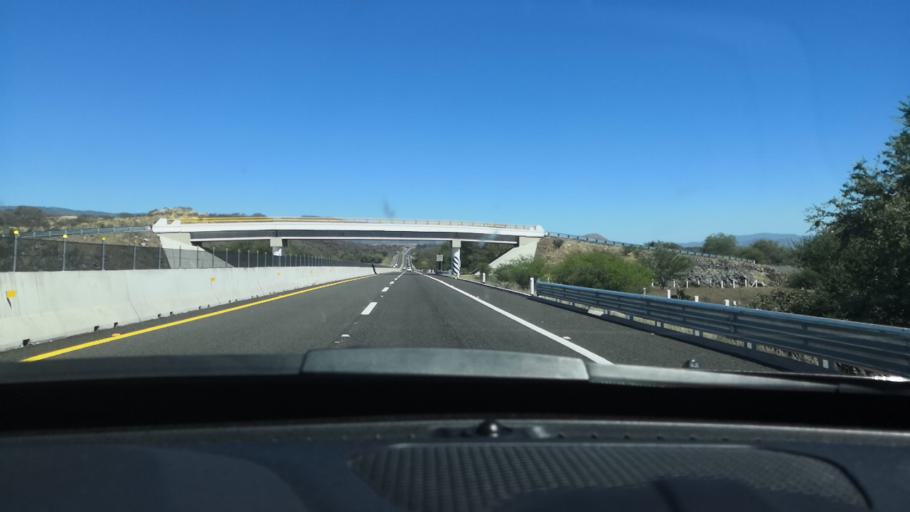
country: MX
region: Nayarit
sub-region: Ahuacatlan
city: Ahuacatlan
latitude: 21.0656
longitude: -104.4934
